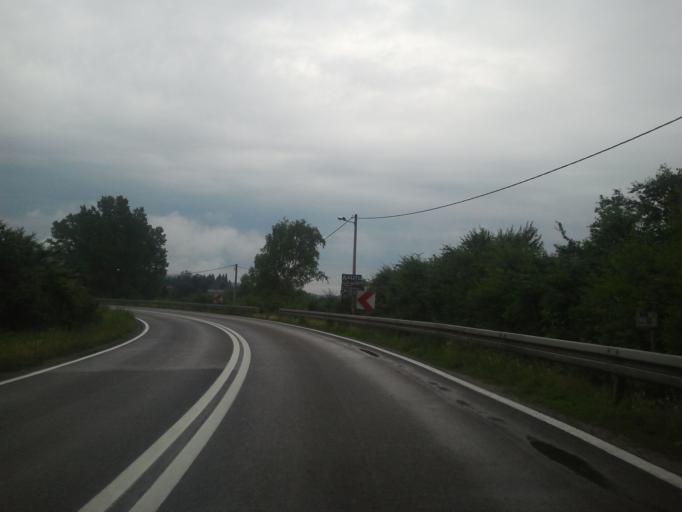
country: HR
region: Karlovacka
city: Vojnic
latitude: 45.3904
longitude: 15.6136
